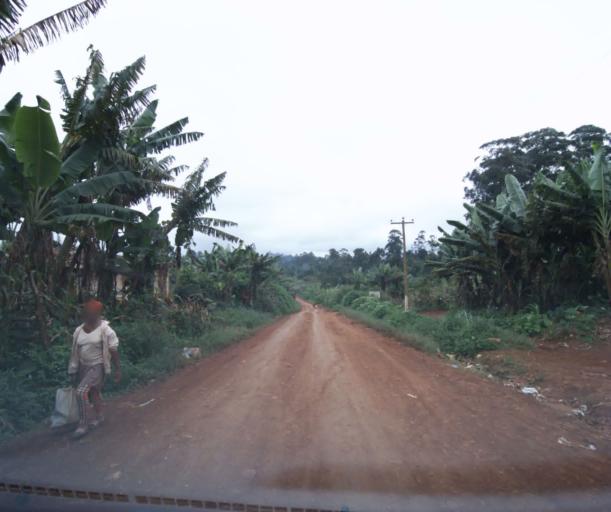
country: CM
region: West
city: Dschang
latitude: 5.5077
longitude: 9.9939
